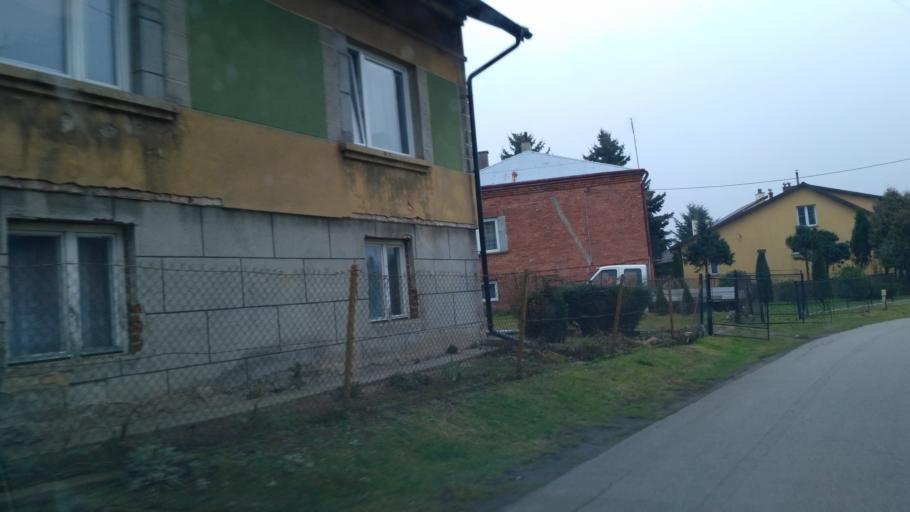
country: PL
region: Subcarpathian Voivodeship
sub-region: Powiat jaroslawski
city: Pawlosiow
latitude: 49.9669
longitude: 22.6478
